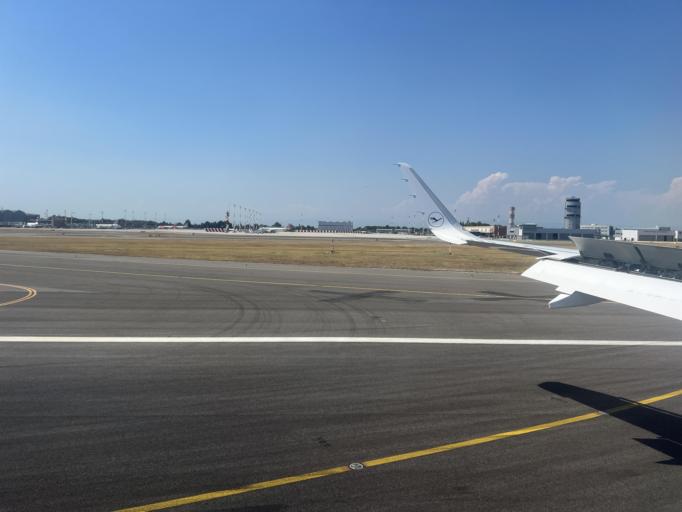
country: IT
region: Veneto
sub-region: Provincia di Venezia
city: Tessera
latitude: 45.5044
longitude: 12.3503
